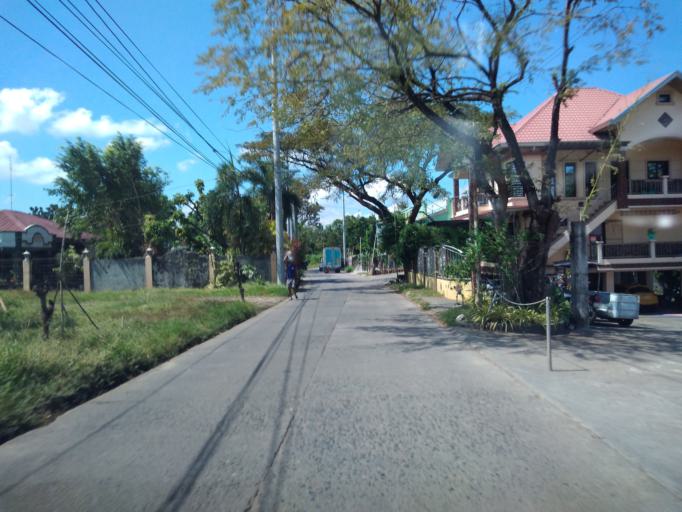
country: PH
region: Central Luzon
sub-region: Province of Bulacan
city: Balasing
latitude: 14.8590
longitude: 121.0292
